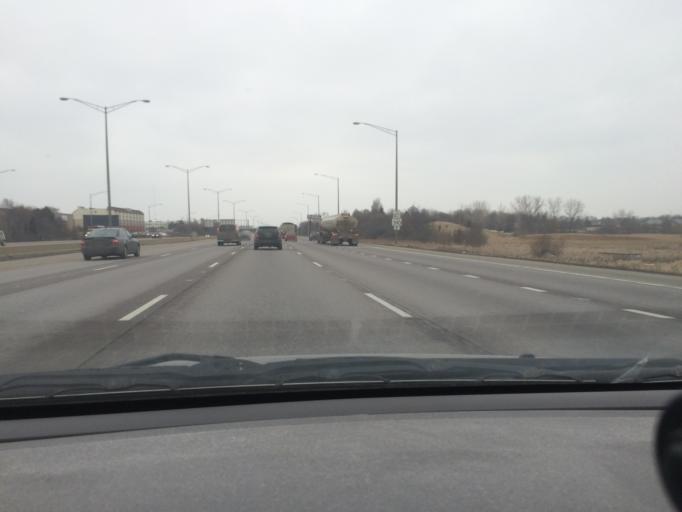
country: US
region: Illinois
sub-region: DuPage County
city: Itasca
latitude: 41.9667
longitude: -88.0254
